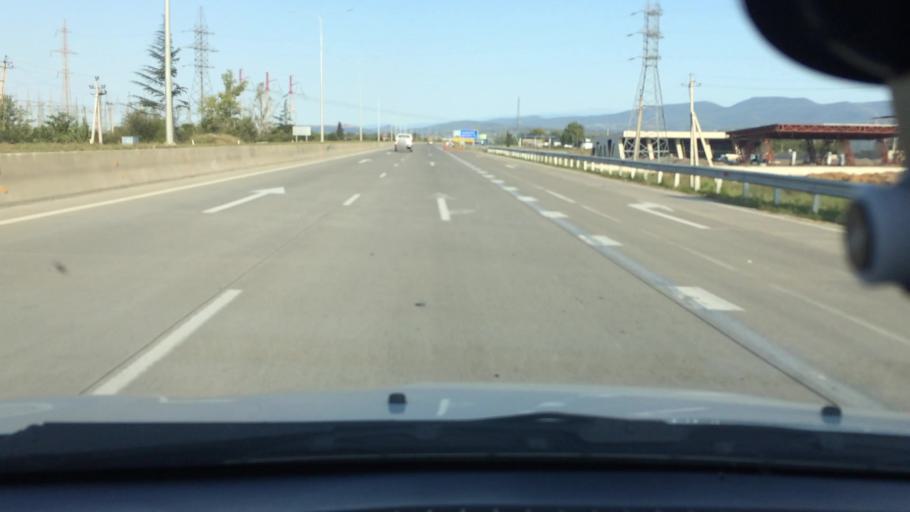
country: GE
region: Imereti
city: Zestap'oni
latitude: 42.1457
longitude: 42.9668
